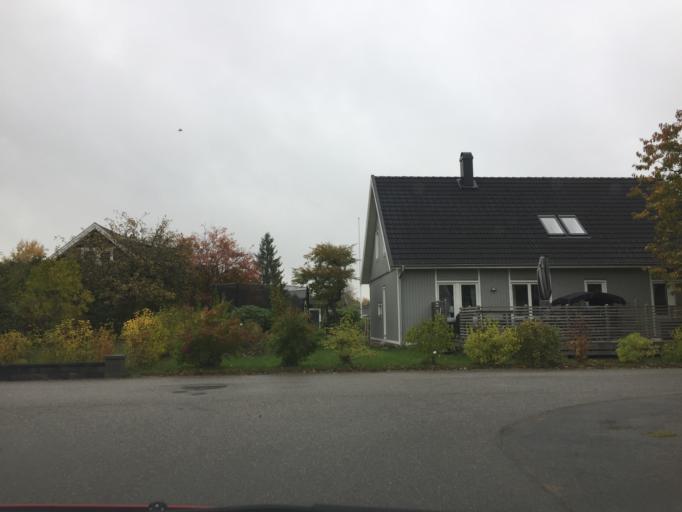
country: SE
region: Vaestra Goetaland
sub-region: Trollhattan
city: Trollhattan
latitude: 58.2294
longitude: 12.3041
